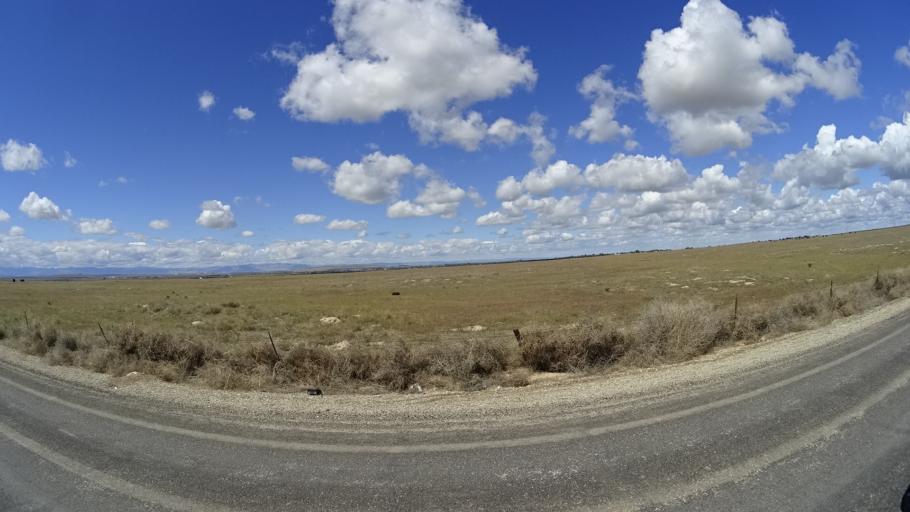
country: US
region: Idaho
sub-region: Ada County
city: Kuna
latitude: 43.4697
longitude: -116.2743
